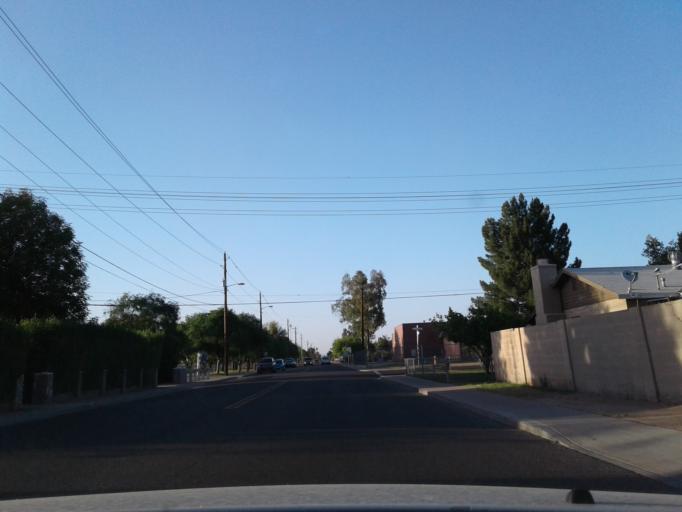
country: US
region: Arizona
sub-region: Maricopa County
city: Glendale
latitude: 33.5308
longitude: -112.1039
